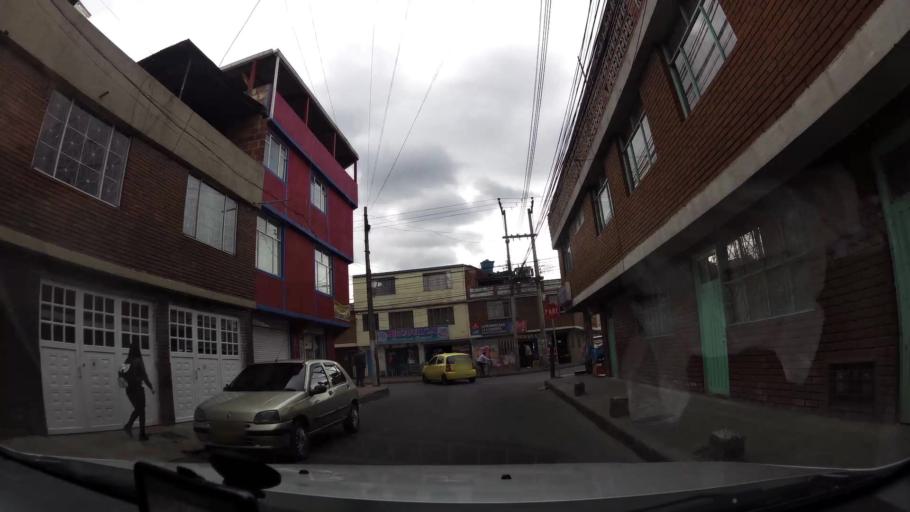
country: CO
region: Bogota D.C.
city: Bogota
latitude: 4.6061
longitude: -74.1341
